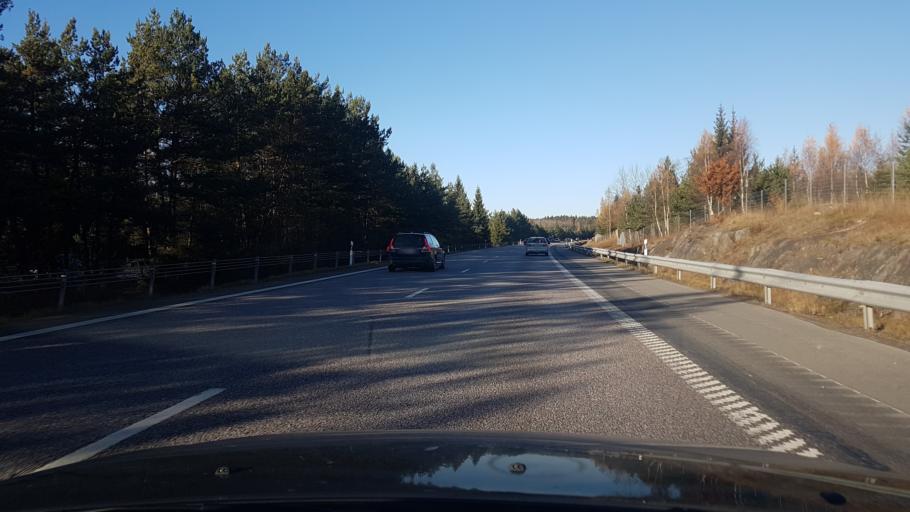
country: SE
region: Uppsala
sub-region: Knivsta Kommun
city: Knivsta
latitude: 59.7042
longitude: 17.8550
